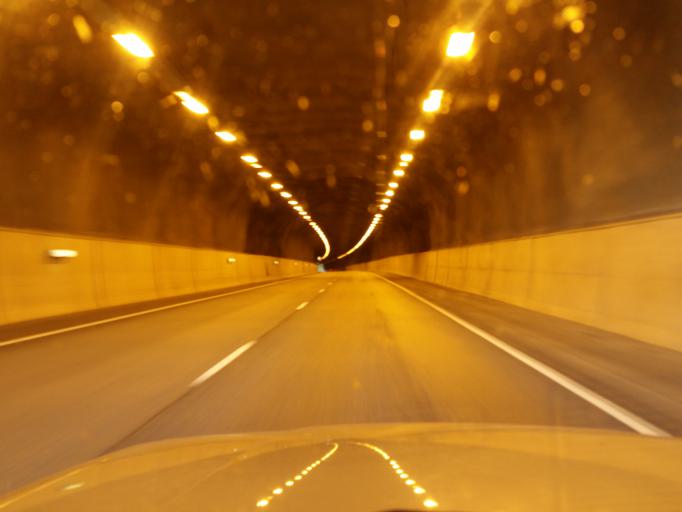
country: FI
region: Varsinais-Suomi
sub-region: Salo
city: Muurla
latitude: 60.3727
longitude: 23.3639
